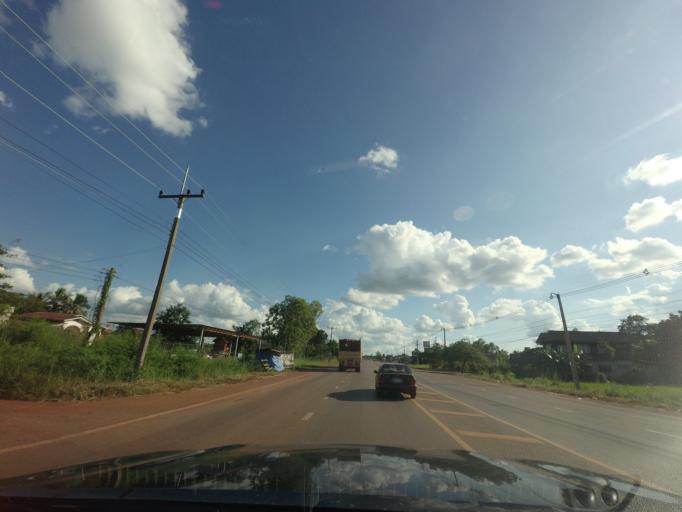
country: TH
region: Changwat Udon Thani
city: Ban Dung
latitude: 17.7292
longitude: 103.2519
